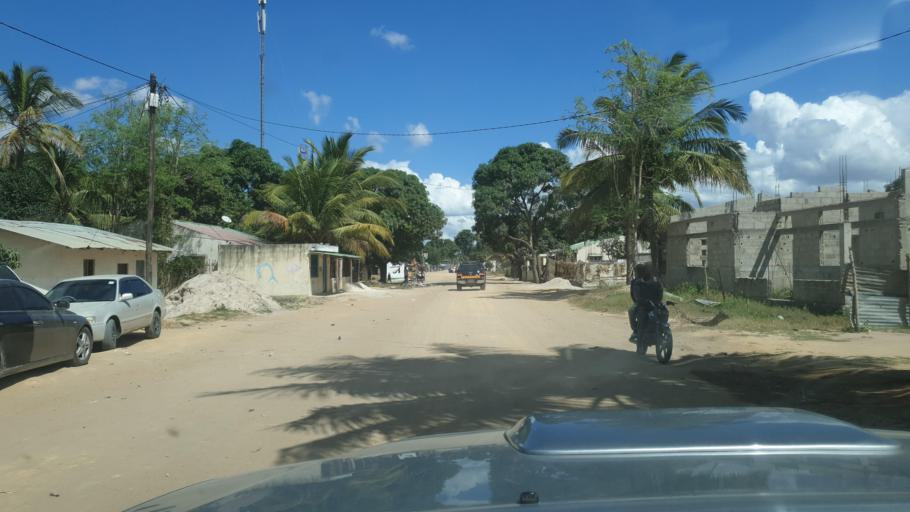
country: MZ
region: Nampula
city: Nacala
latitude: -14.5710
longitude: 40.6937
